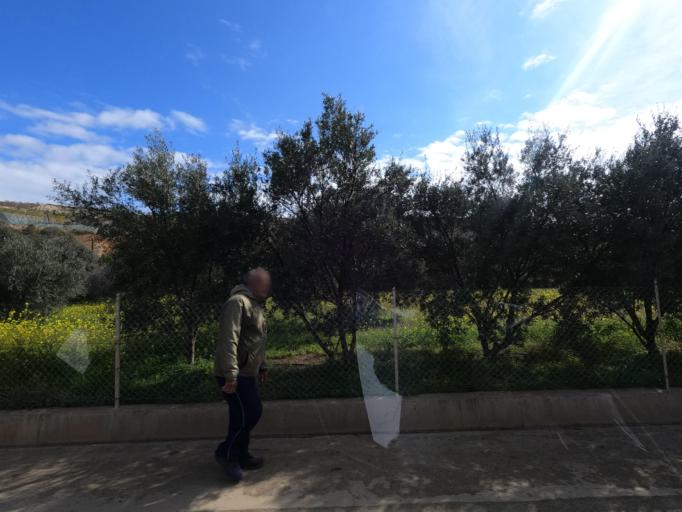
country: CY
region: Lefkosia
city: Lefka
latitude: 35.0881
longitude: 32.8889
